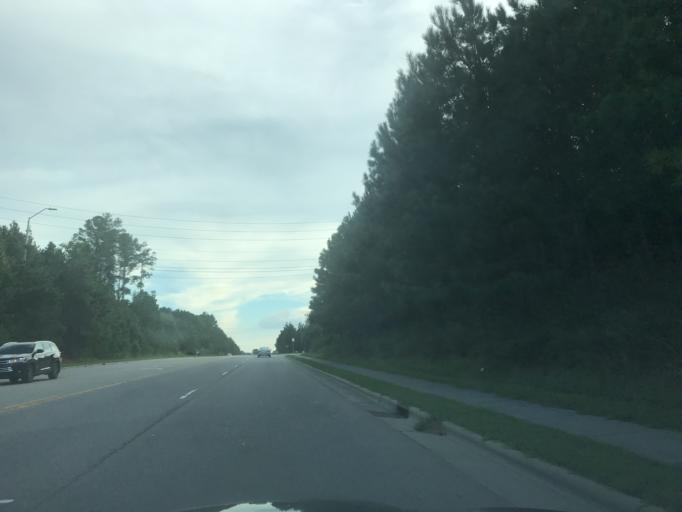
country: US
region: North Carolina
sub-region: Wake County
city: Green Level
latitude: 35.7776
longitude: -78.8726
